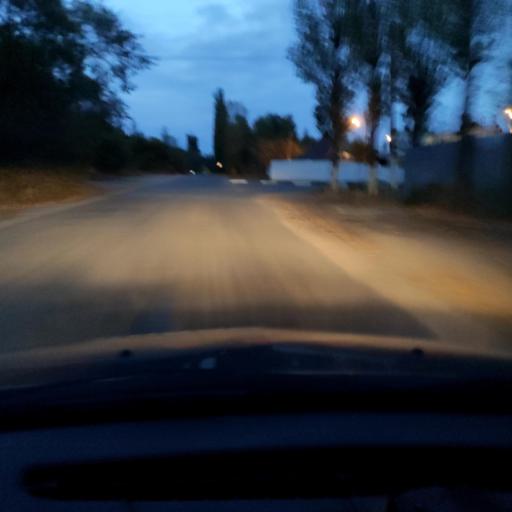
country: RU
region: Voronezj
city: Pridonskoy
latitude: 51.6753
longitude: 39.0969
